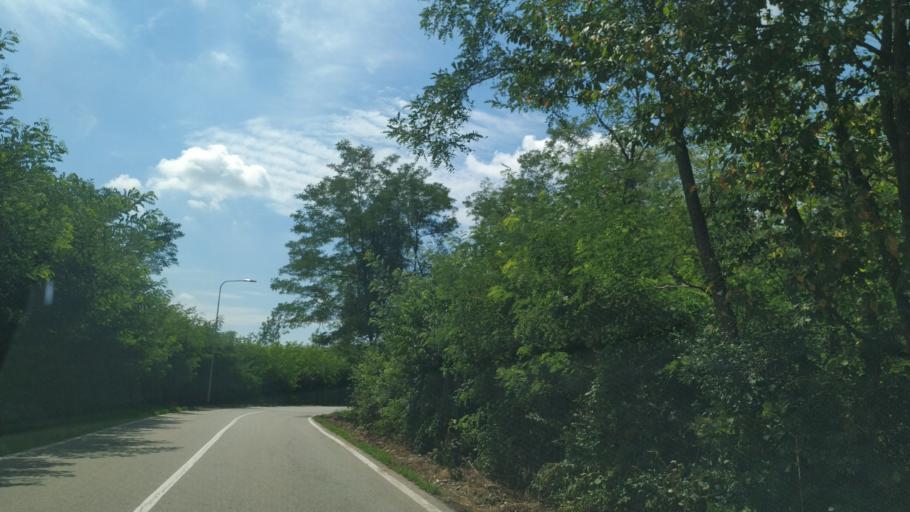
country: IT
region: Piedmont
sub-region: Provincia di Novara
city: Briga Novarese
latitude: 45.7158
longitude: 8.4506
